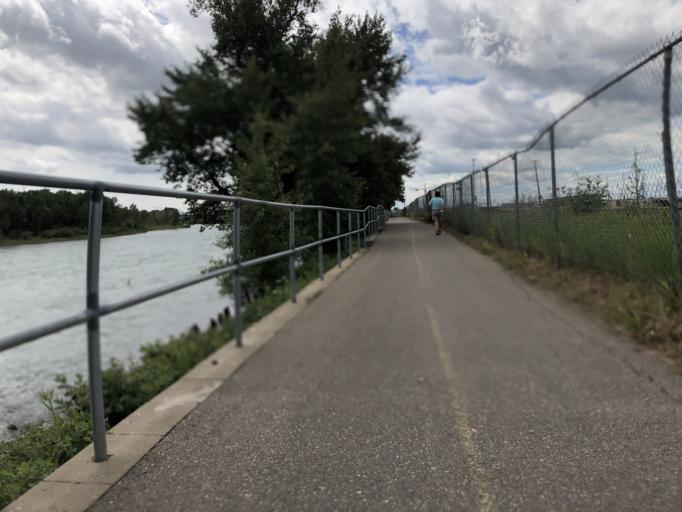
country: CA
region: Alberta
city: Calgary
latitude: 51.0218
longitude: -114.0122
